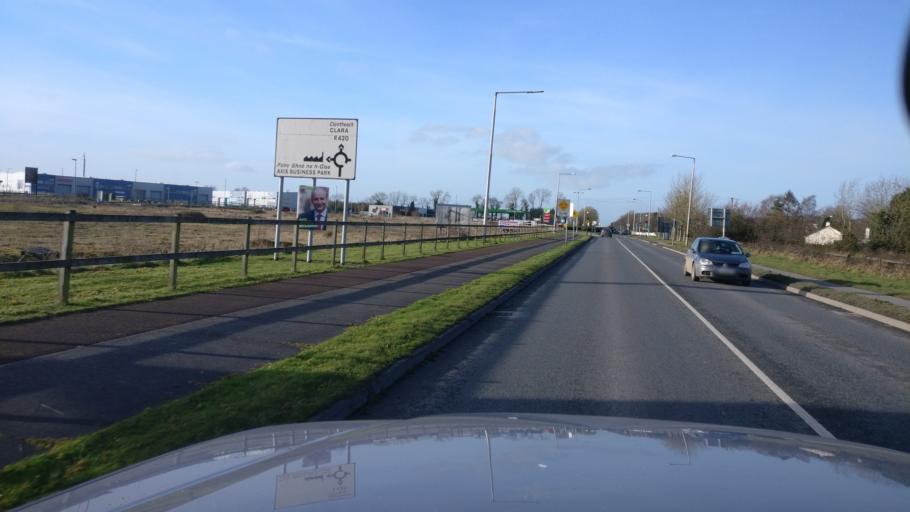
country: IE
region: Leinster
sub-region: Uibh Fhaili
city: Tullamore
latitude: 53.2883
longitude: -7.5118
